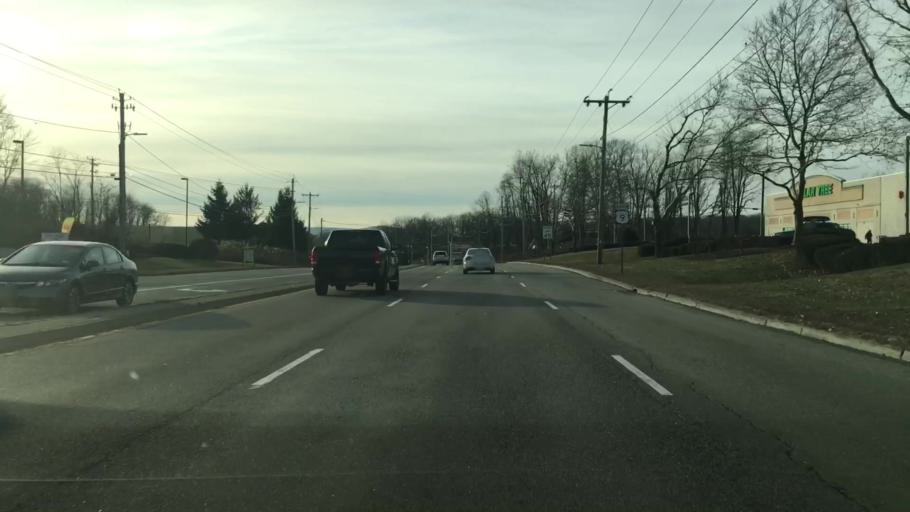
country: US
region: New York
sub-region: Dutchess County
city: Crown Heights
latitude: 41.6216
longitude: -73.9175
